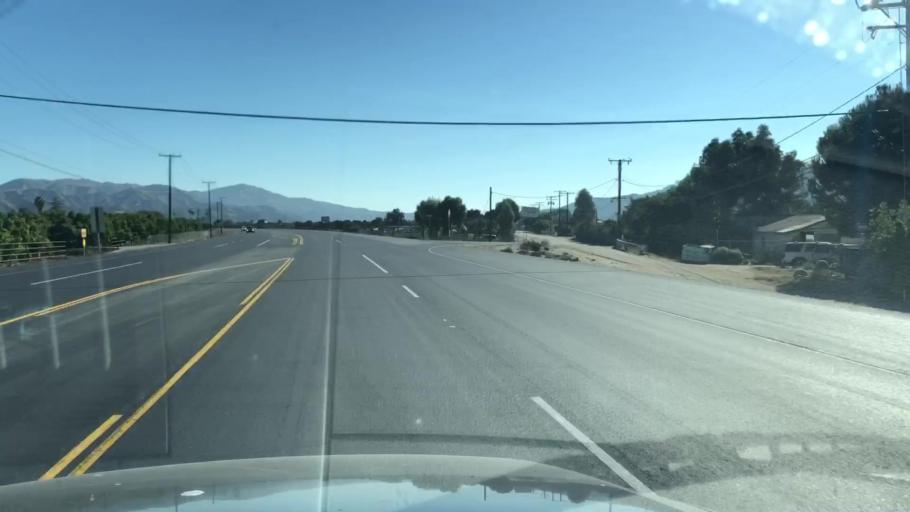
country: US
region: California
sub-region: Ventura County
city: Piru
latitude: 34.4010
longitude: -118.8058
